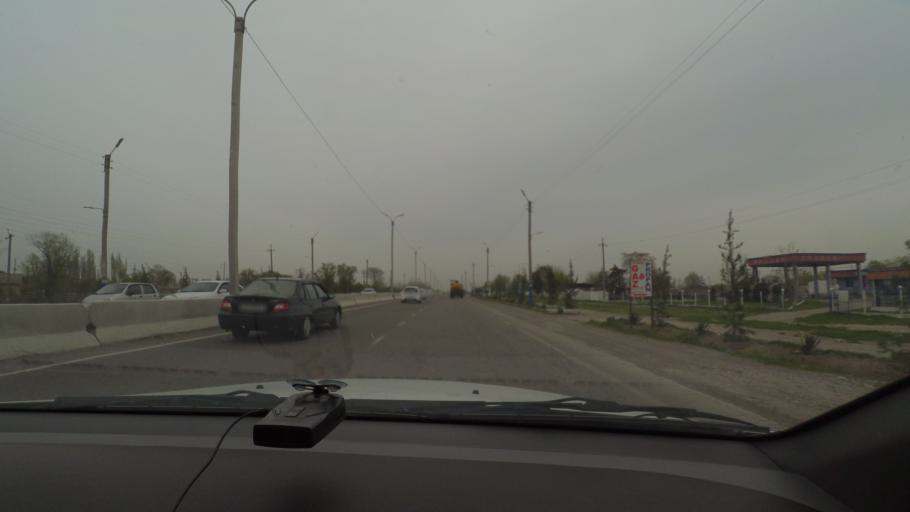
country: KZ
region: Ongtustik Qazaqstan
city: Myrzakent
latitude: 40.5407
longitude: 68.4203
